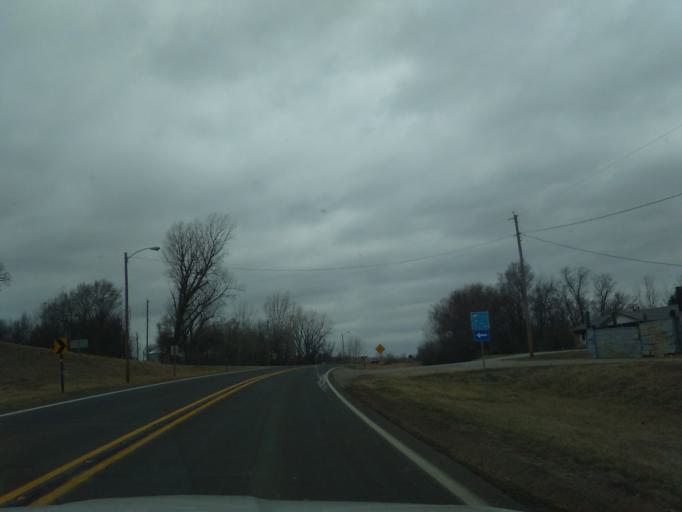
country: US
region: Nebraska
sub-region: Richardson County
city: Falls City
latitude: 40.0532
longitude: -95.4327
